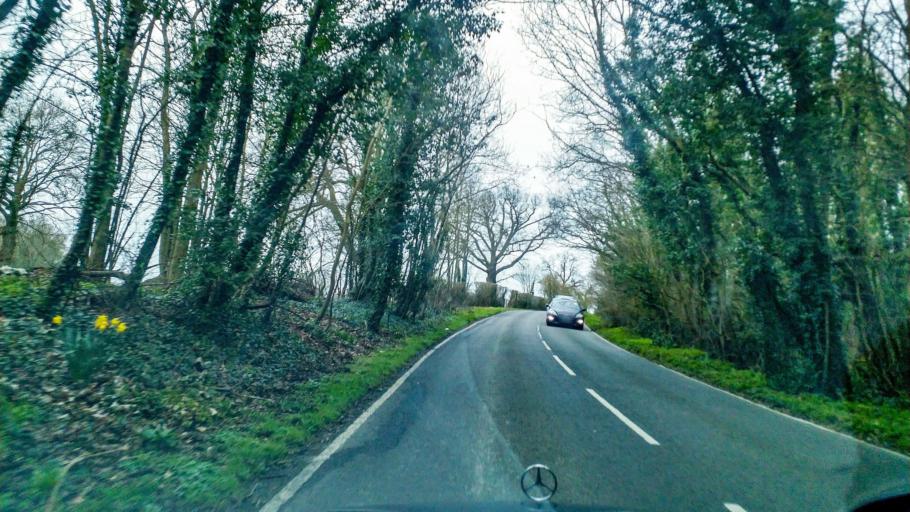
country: GB
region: England
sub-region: Surrey
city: Salfords
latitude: 51.1797
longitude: -0.2071
